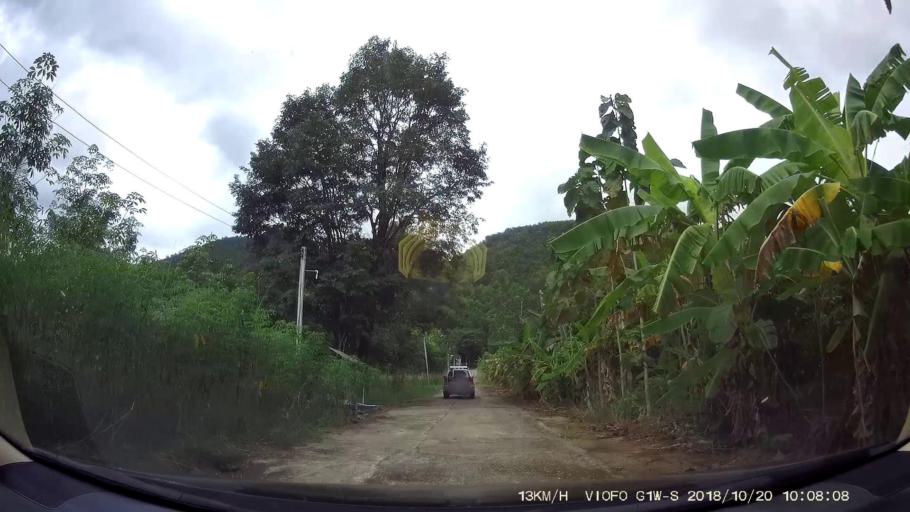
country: TH
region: Chaiyaphum
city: Khon San
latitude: 16.5501
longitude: 101.8520
